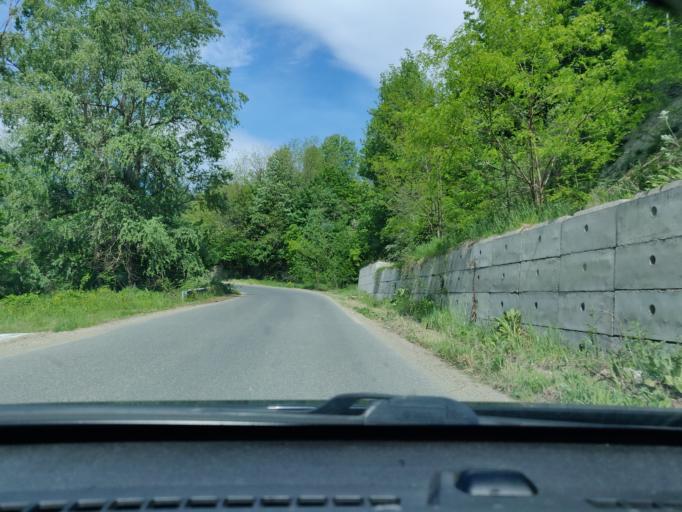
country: RO
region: Vrancea
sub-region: Comuna Vidra
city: Vidra
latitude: 45.9330
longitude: 26.8885
